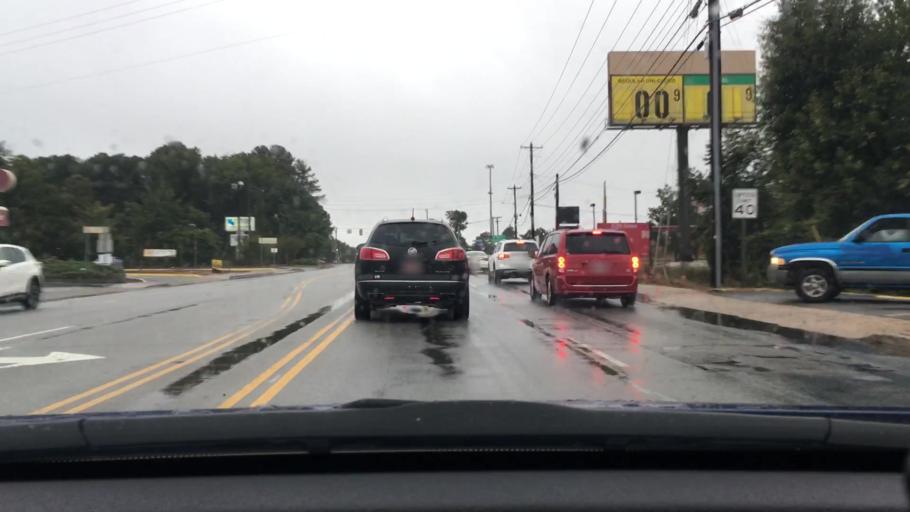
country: US
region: South Carolina
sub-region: Lexington County
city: Saint Andrews
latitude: 34.0376
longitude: -81.0913
